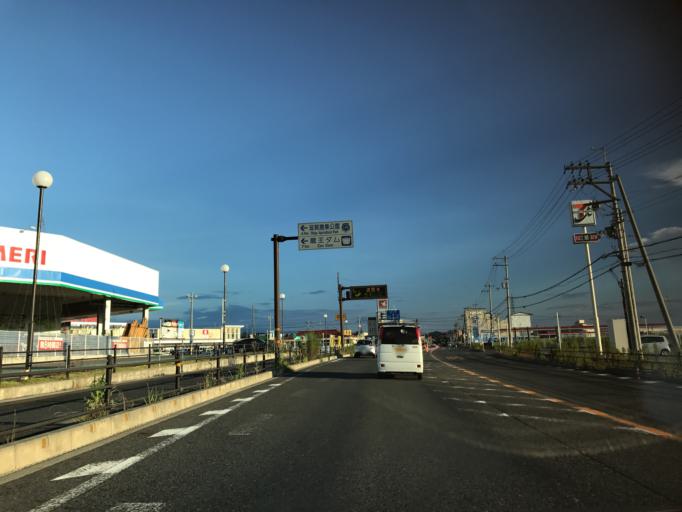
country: JP
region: Shiga Prefecture
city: Hino
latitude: 35.0230
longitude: 136.2391
